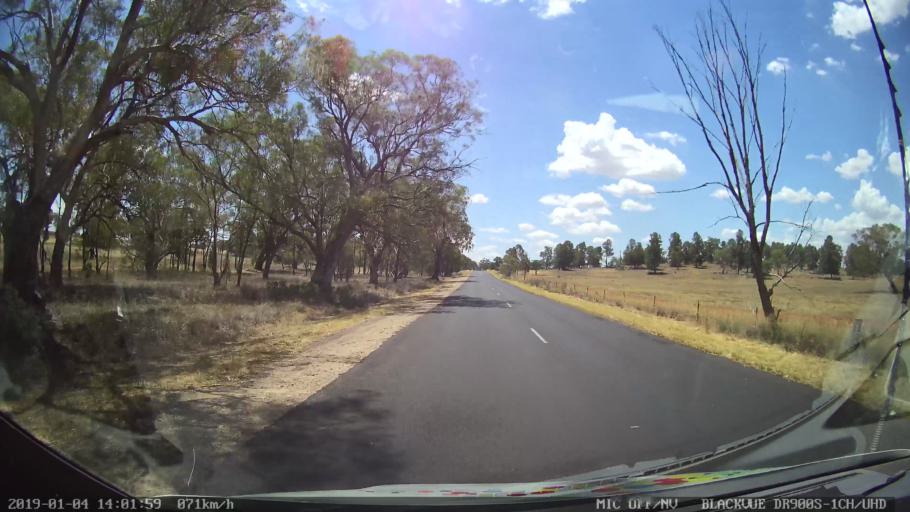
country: AU
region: New South Wales
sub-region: Dubbo Municipality
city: Dubbo
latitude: -32.2910
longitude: 148.5984
